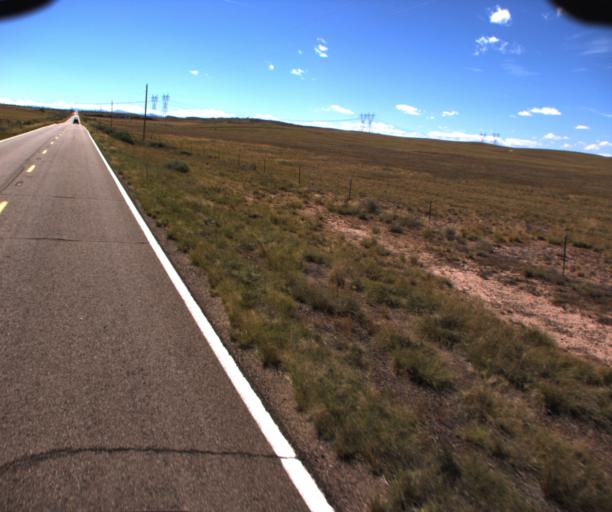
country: US
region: Arizona
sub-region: Apache County
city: Saint Johns
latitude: 34.5851
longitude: -109.3313
